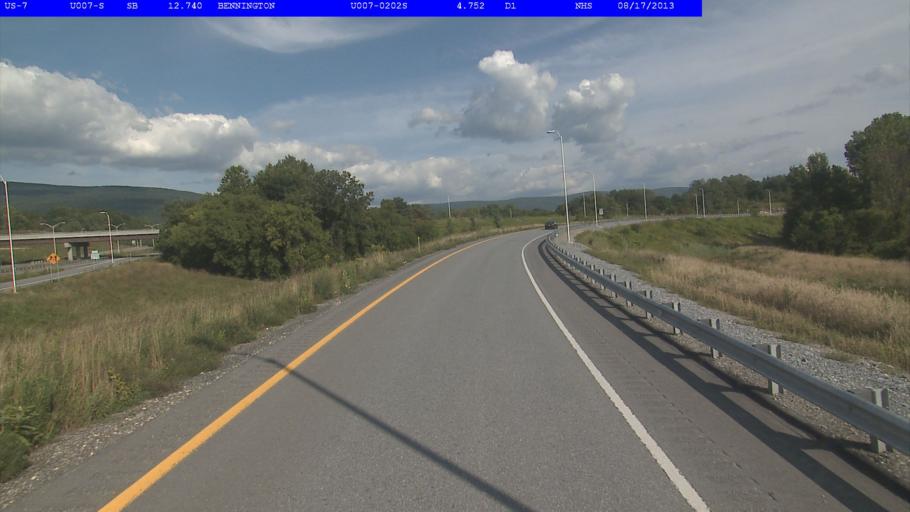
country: US
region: Vermont
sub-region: Bennington County
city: Bennington
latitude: 42.9020
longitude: -73.2021
